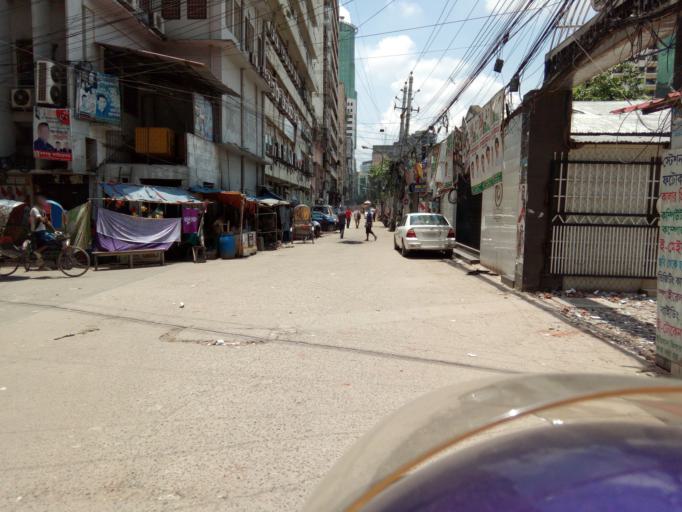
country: BD
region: Dhaka
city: Paltan
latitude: 23.7279
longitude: 90.4206
